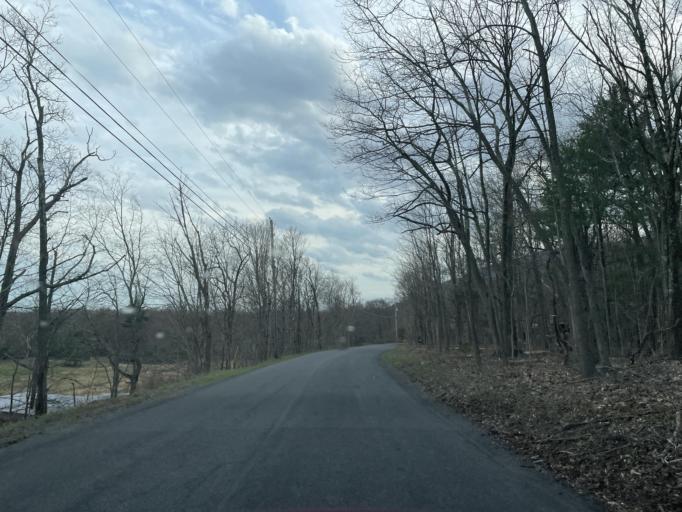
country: US
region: New York
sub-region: Ulster County
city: Manorville
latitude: 42.1217
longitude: -74.0451
